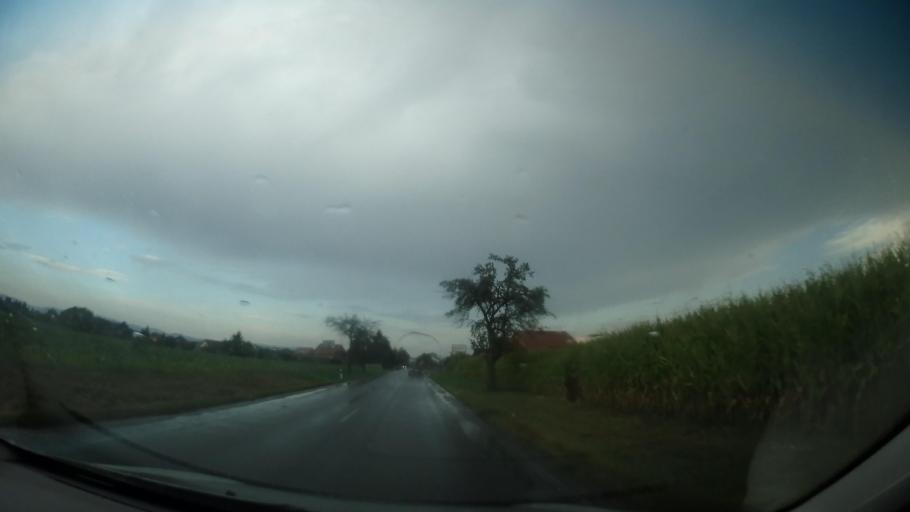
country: CZ
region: Olomoucky
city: Ujezd
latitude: 49.7159
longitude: 17.1533
